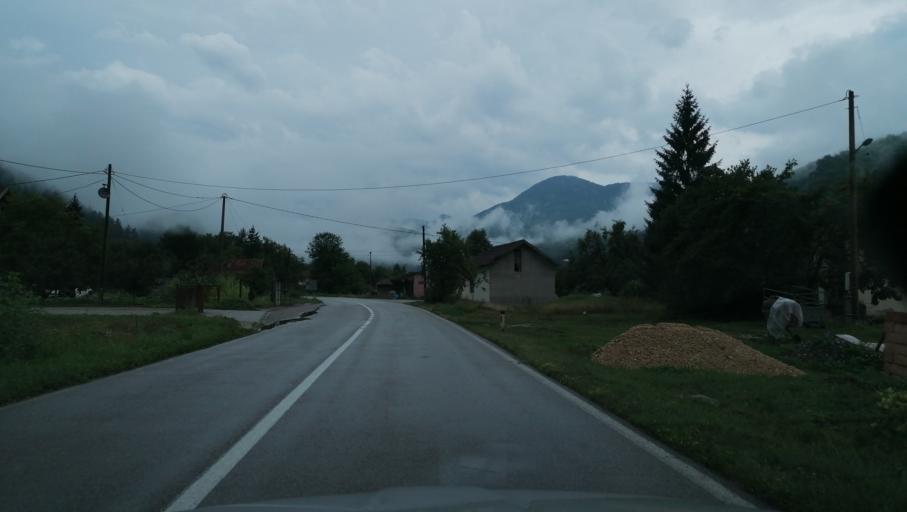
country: RS
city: Durici
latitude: 43.7564
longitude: 19.3872
